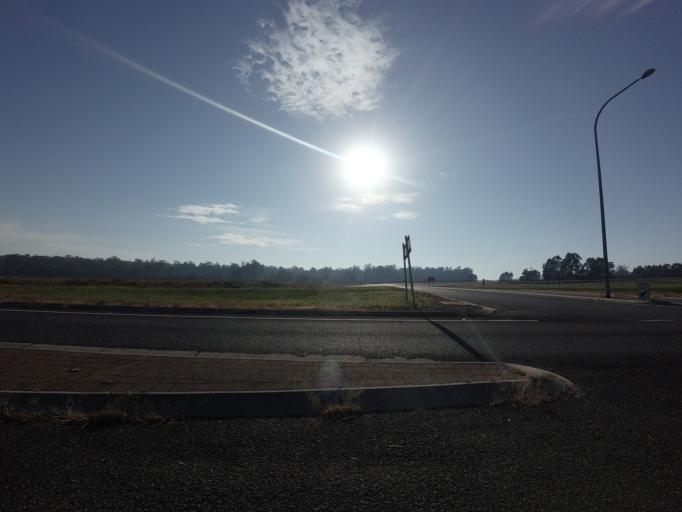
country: AU
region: Tasmania
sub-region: Northern Midlands
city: Longford
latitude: -41.5346
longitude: 147.0446
